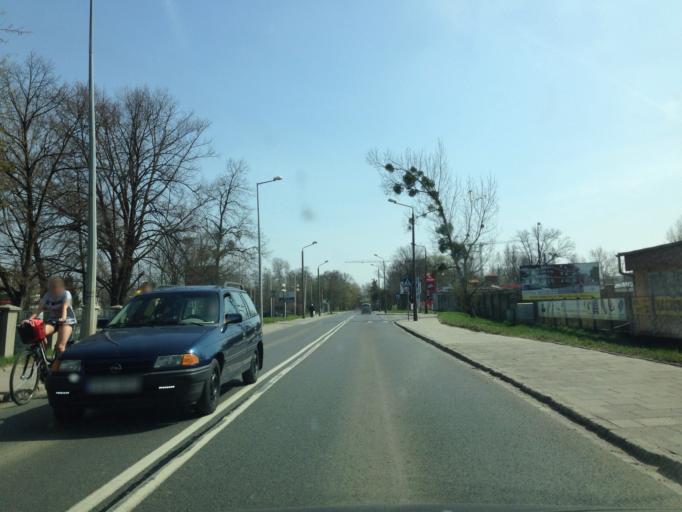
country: PL
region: Lower Silesian Voivodeship
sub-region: Powiat wroclawski
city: Wilczyce
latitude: 51.1147
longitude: 17.1150
